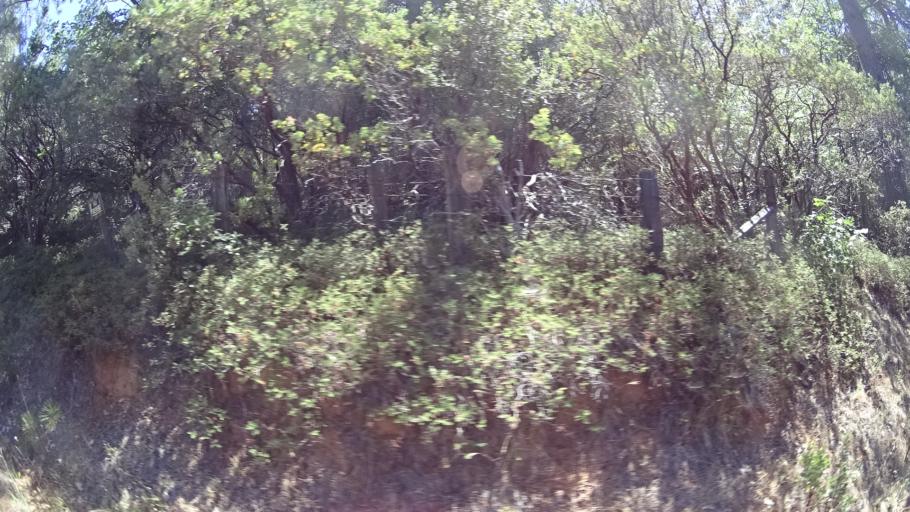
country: US
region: California
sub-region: Amador County
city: Pioneer
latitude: 38.4281
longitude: -120.4928
